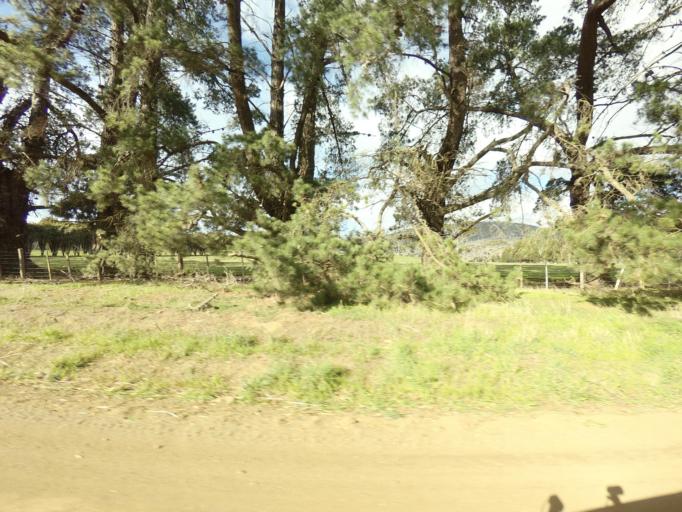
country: AU
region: Tasmania
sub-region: Derwent Valley
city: New Norfolk
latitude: -42.7133
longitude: 146.8888
